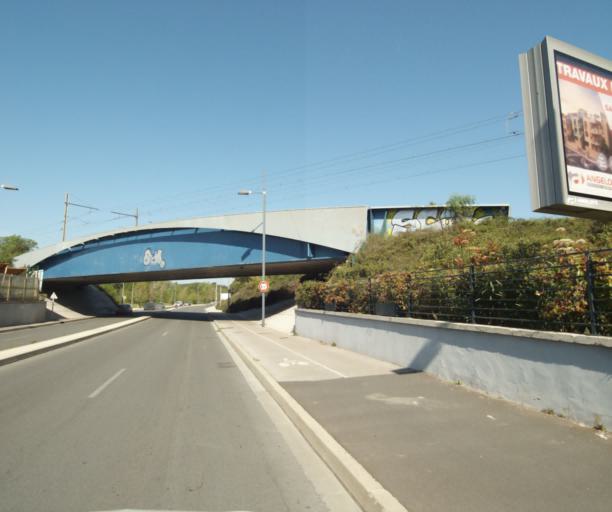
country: FR
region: Languedoc-Roussillon
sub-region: Departement de l'Herault
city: Castelnau-le-Lez
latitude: 43.6266
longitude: 3.9003
